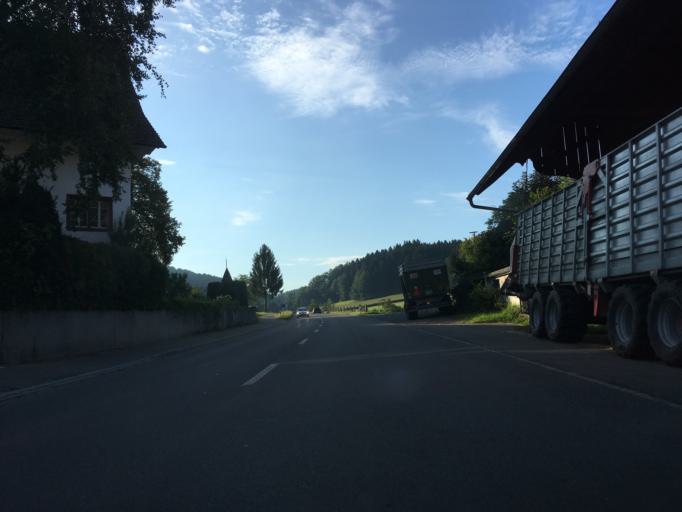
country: CH
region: Zurich
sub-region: Bezirk Affoltern
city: Hausen am Albis / Hausen (Dorf)
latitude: 47.2616
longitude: 8.5184
